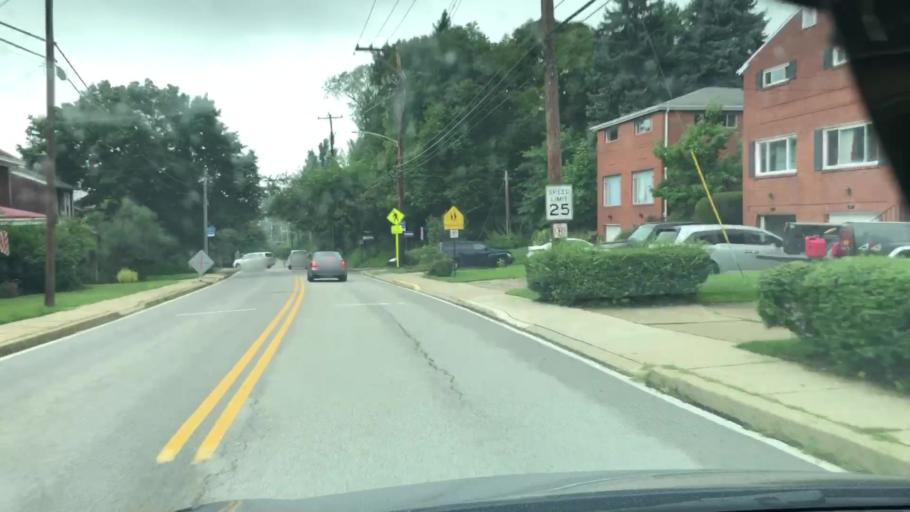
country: US
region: Pennsylvania
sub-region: Allegheny County
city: Dormont
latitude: 40.3865
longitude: -80.0472
